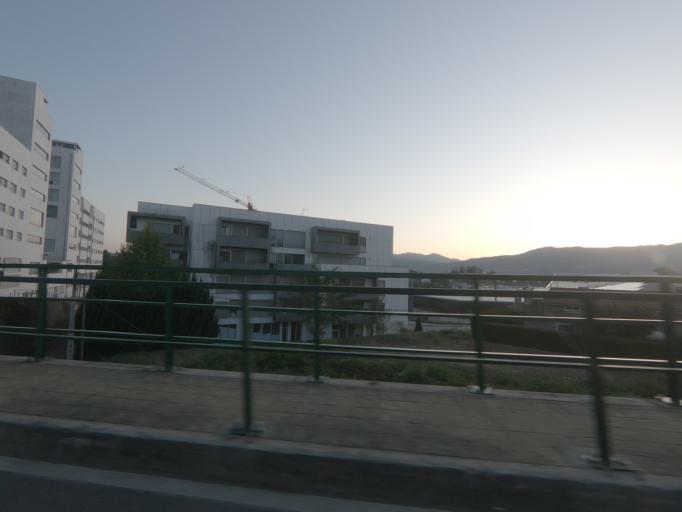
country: PT
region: Vila Real
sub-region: Vila Real
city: Vila Real
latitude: 41.2965
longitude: -7.7318
